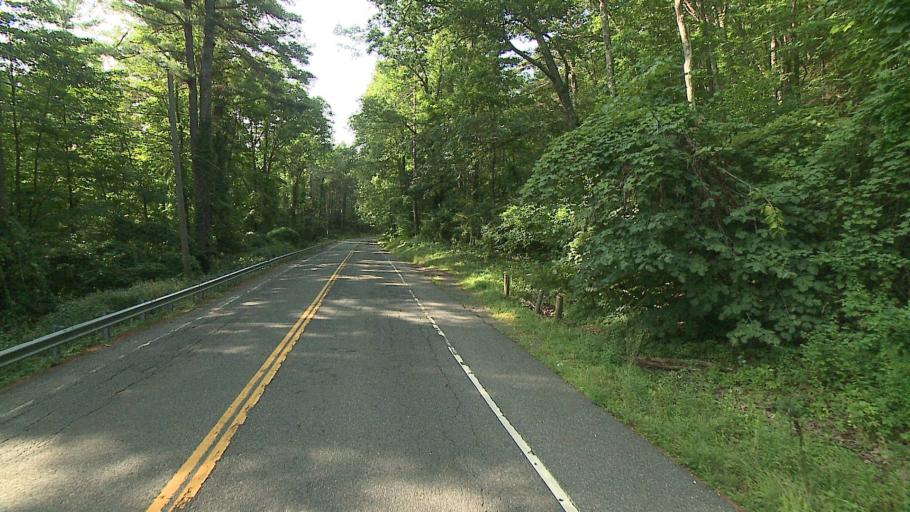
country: US
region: Connecticut
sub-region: Litchfield County
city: Canaan
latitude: 41.9119
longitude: -73.3646
